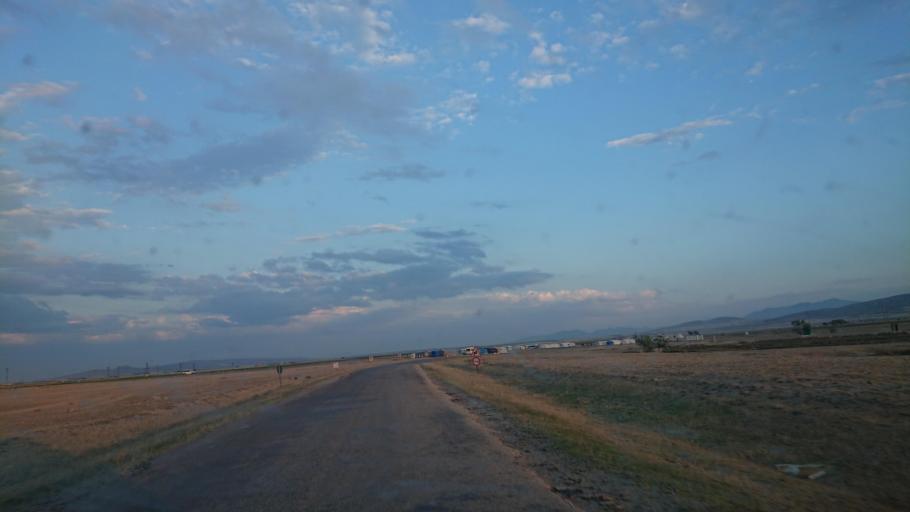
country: TR
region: Aksaray
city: Agacoren
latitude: 38.8893
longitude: 34.0552
